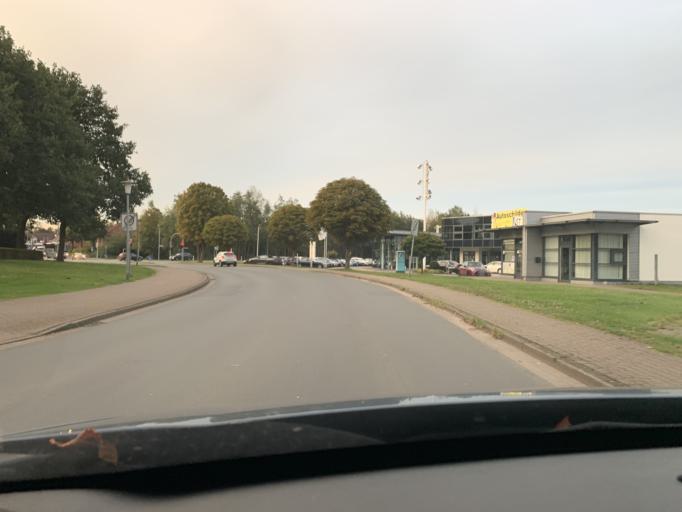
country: DE
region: Lower Saxony
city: Westerstede
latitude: 53.2564
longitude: 7.9359
